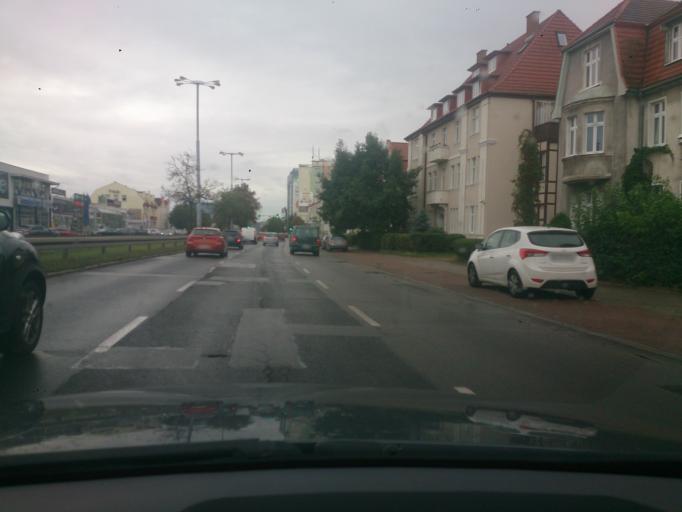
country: PL
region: Pomeranian Voivodeship
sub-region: Sopot
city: Sopot
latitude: 54.4083
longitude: 18.5689
